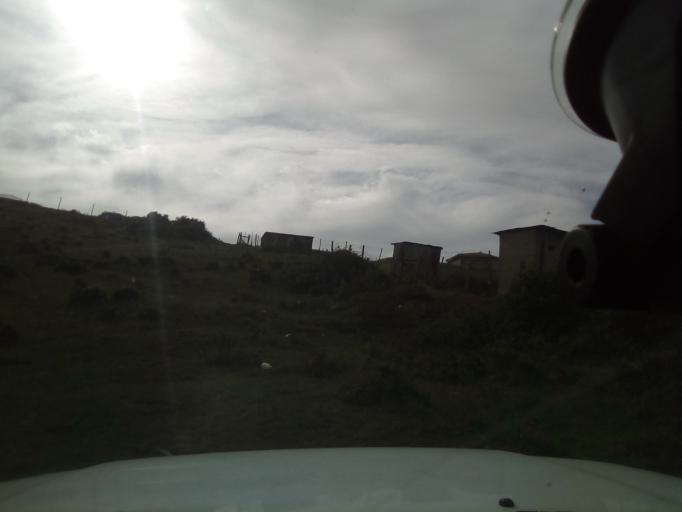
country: ZA
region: Eastern Cape
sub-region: Buffalo City Metropolitan Municipality
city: East London
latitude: -32.7952
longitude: 27.9673
